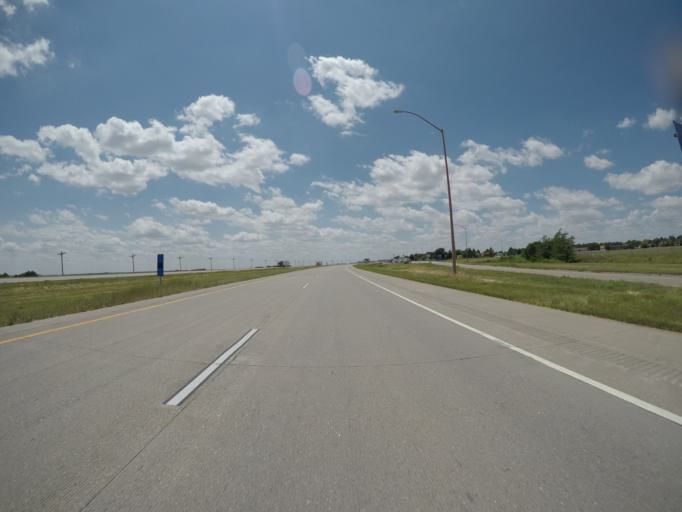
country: US
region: Colorado
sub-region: Kit Carson County
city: Burlington
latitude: 39.2968
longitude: -102.2620
